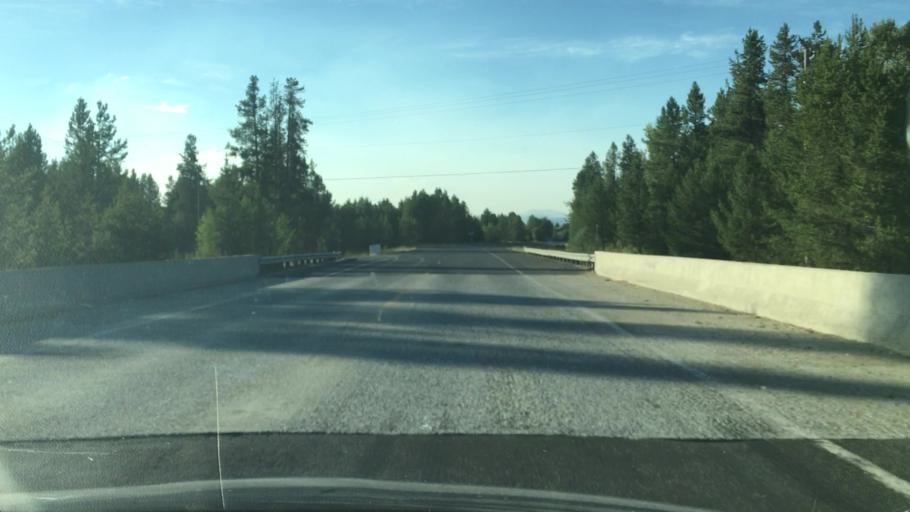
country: US
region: Idaho
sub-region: Valley County
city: McCall
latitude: 44.7887
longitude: -116.0772
